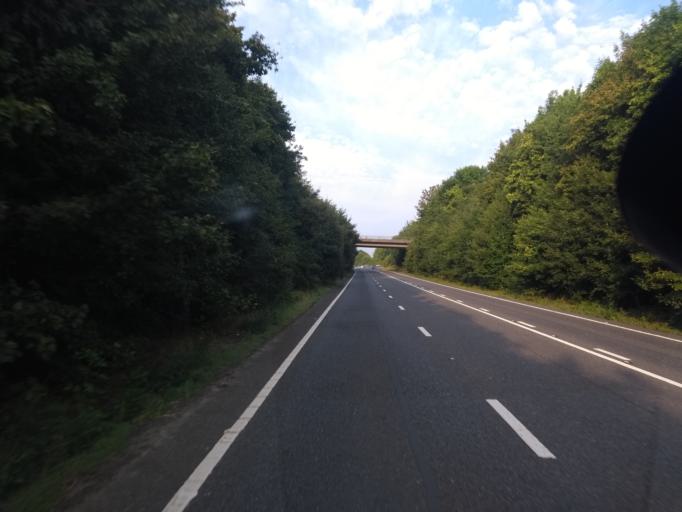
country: GB
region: England
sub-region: Somerset
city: Ilminster
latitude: 50.9302
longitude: -2.9446
